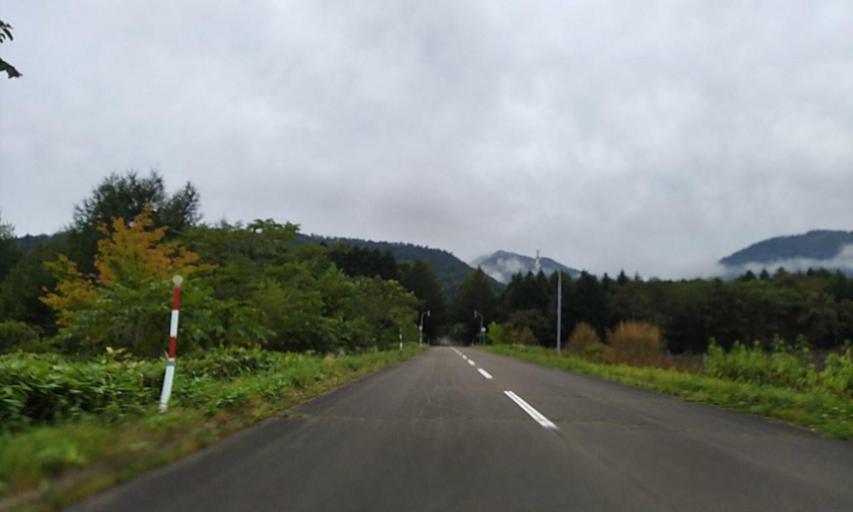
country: JP
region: Hokkaido
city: Bihoro
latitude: 43.5866
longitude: 144.2693
